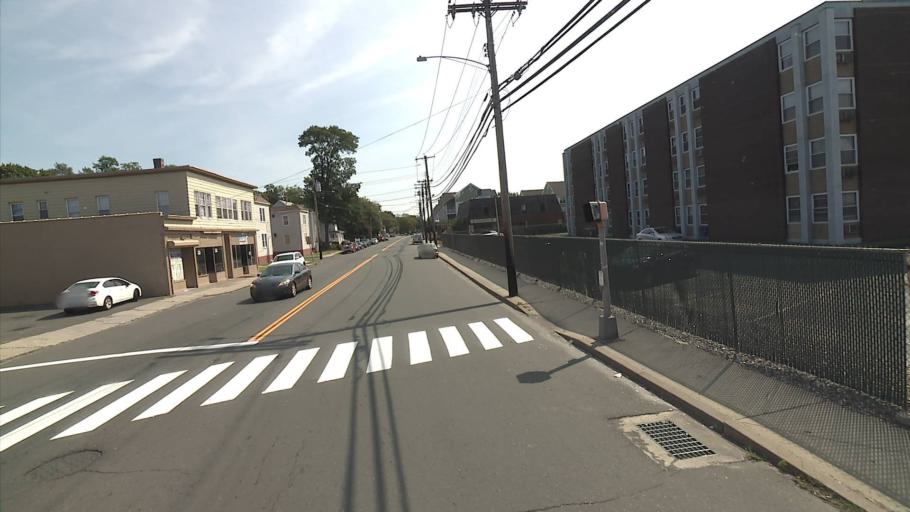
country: US
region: Connecticut
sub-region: Fairfield County
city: Stratford
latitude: 41.1870
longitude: -73.1338
